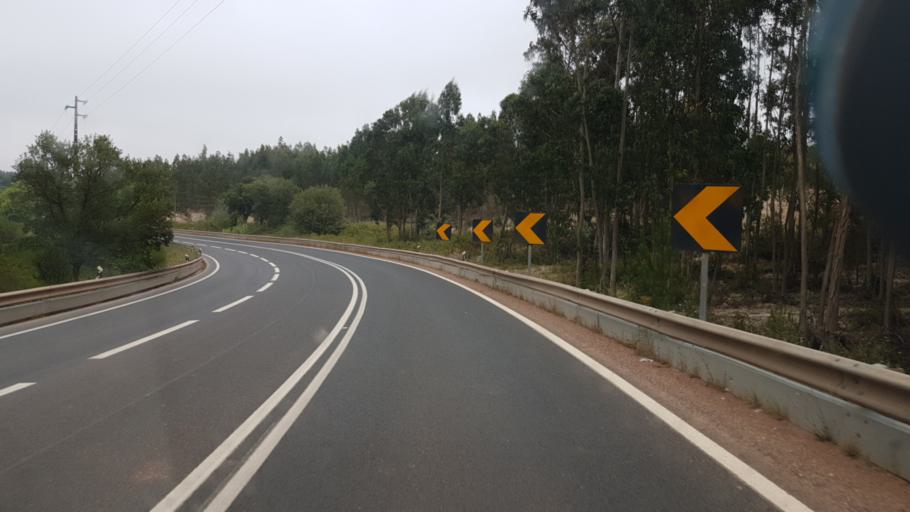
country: PT
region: Lisbon
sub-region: Torres Vedras
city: Torres Vedras
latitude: 39.1613
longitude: -9.2125
